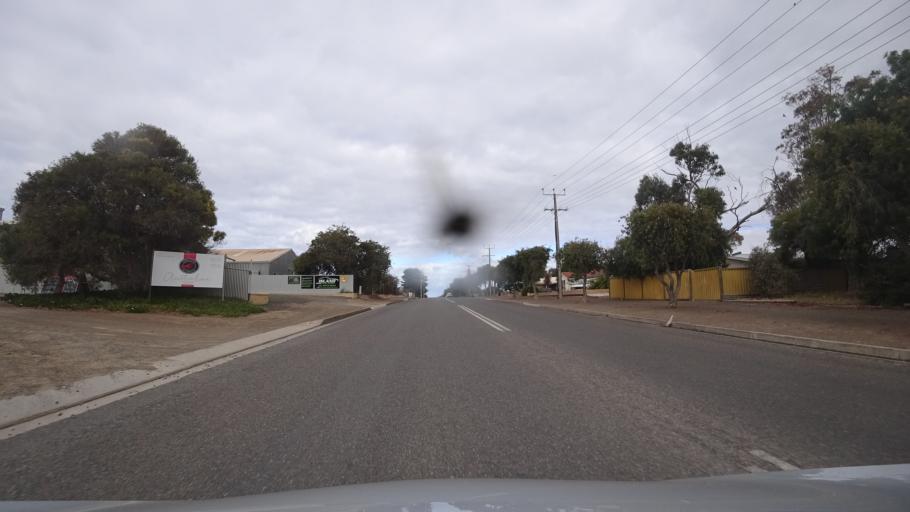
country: AU
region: South Australia
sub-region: Kangaroo Island
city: Kingscote
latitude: -35.6524
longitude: 137.6286
